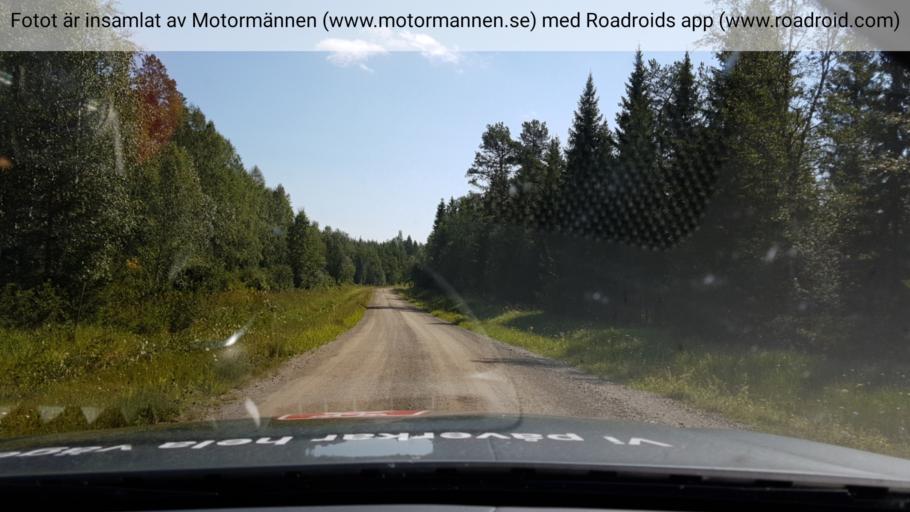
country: SE
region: Jaemtland
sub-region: Stroemsunds Kommun
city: Stroemsund
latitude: 63.3187
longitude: 15.4785
